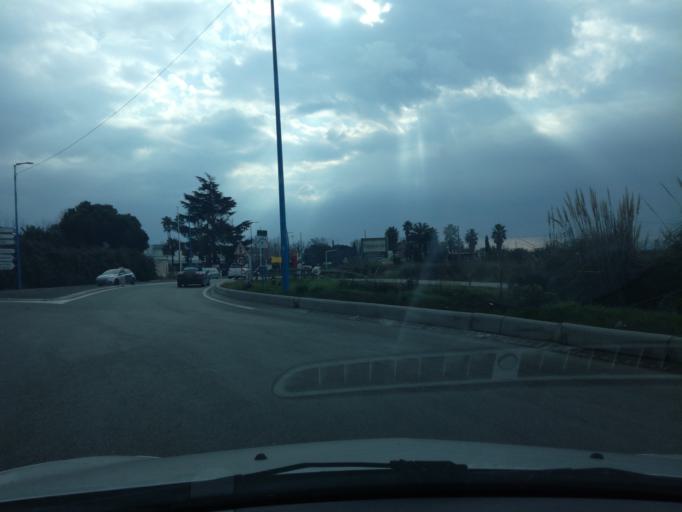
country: FR
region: Provence-Alpes-Cote d'Azur
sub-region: Departement des Alpes-Maritimes
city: Mandelieu-la-Napoule
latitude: 43.5608
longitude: 6.9505
